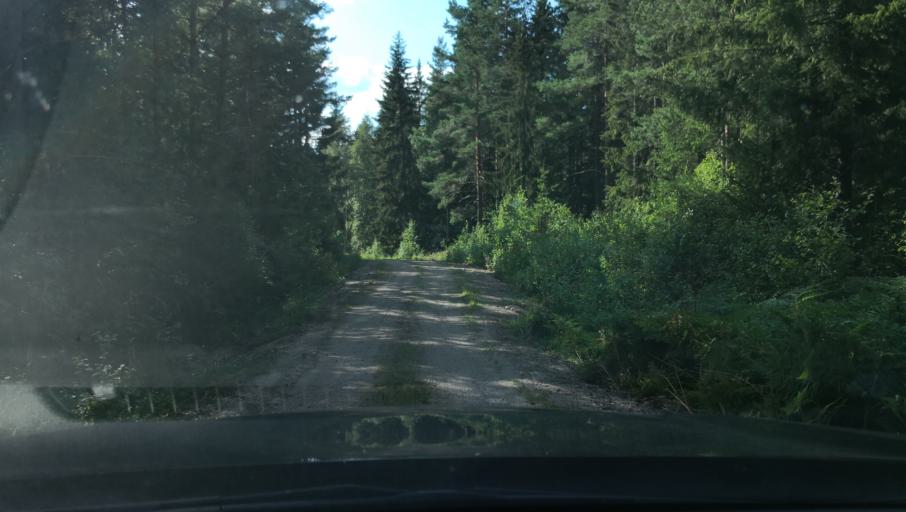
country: SE
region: Vaestmanland
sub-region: Vasteras
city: Skultuna
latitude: 59.7231
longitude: 16.3302
